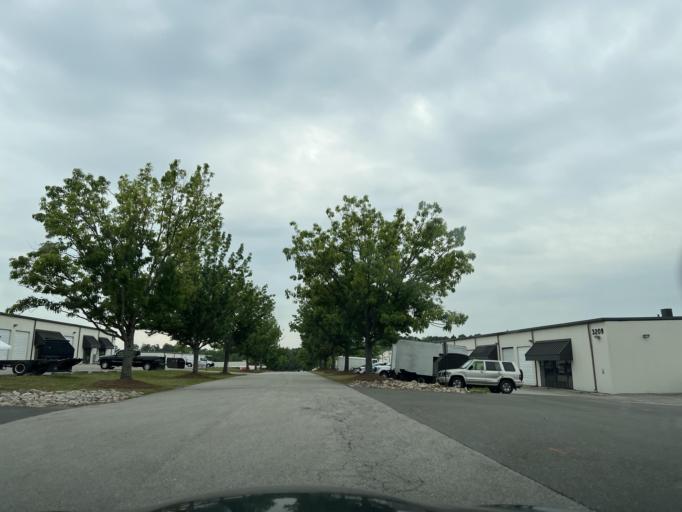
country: US
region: North Carolina
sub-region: Wake County
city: Wake Forest
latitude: 35.8871
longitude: -78.5800
